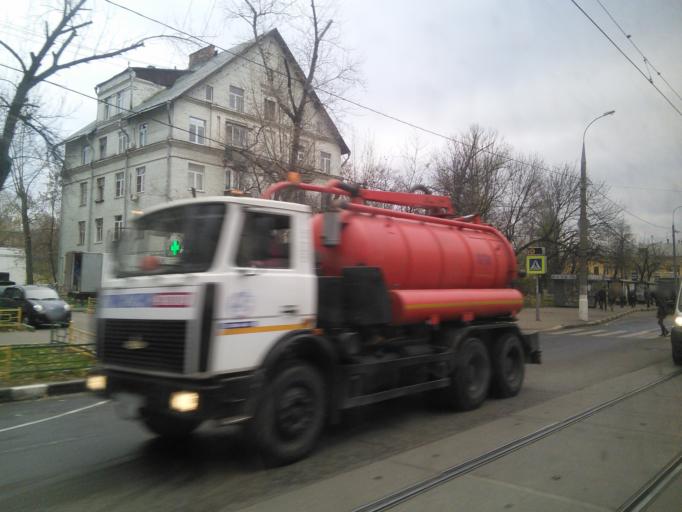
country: RU
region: Moscow
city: Lefortovo
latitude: 55.7562
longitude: 37.7163
